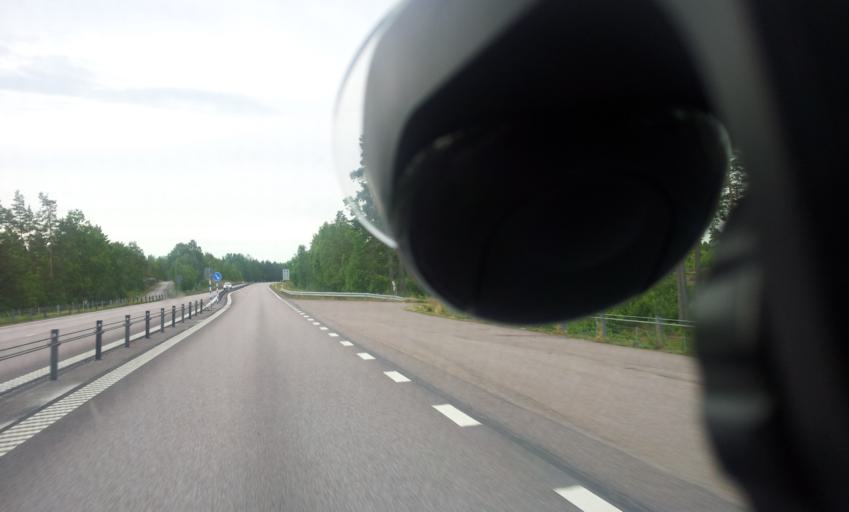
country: SE
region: Kalmar
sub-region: Oskarshamns Kommun
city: Paskallavik
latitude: 57.2099
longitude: 16.4356
